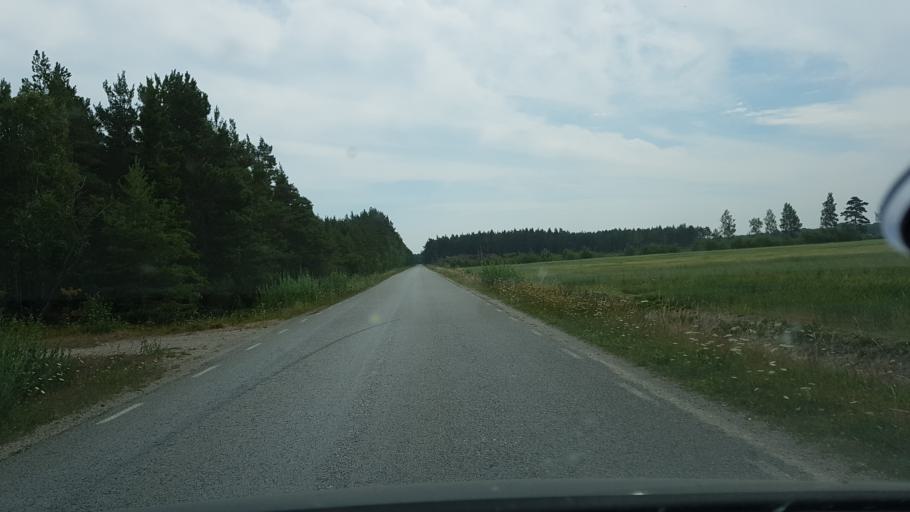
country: SE
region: Gotland
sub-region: Gotland
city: Visby
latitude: 57.7274
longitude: 18.5067
